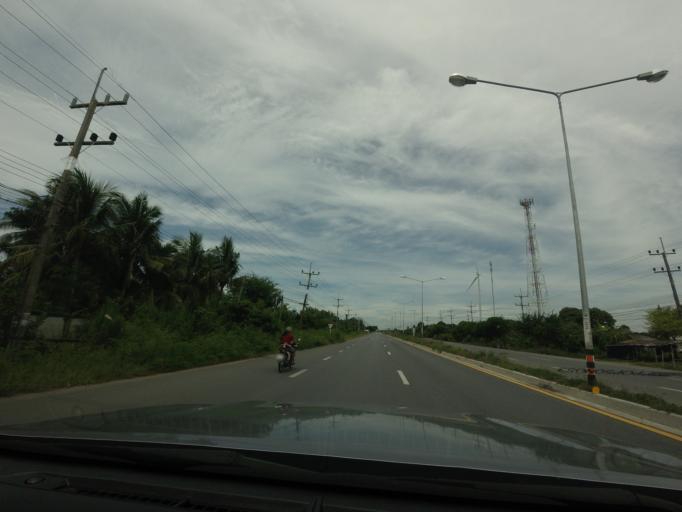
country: TH
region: Songkhla
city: Ranot
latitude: 7.8487
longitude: 100.3519
